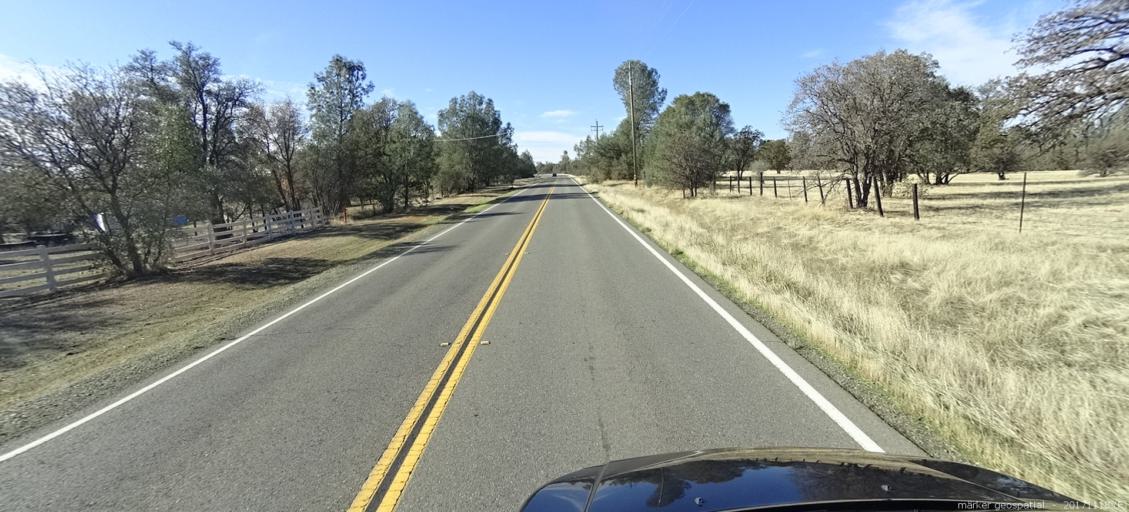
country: US
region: California
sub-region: Shasta County
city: Anderson
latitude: 40.4430
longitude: -122.3686
